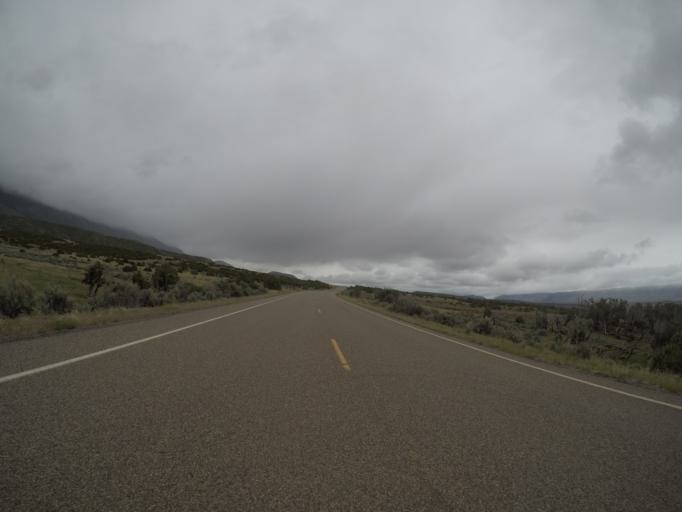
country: US
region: Wyoming
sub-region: Big Horn County
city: Lovell
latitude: 45.0893
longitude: -108.2511
